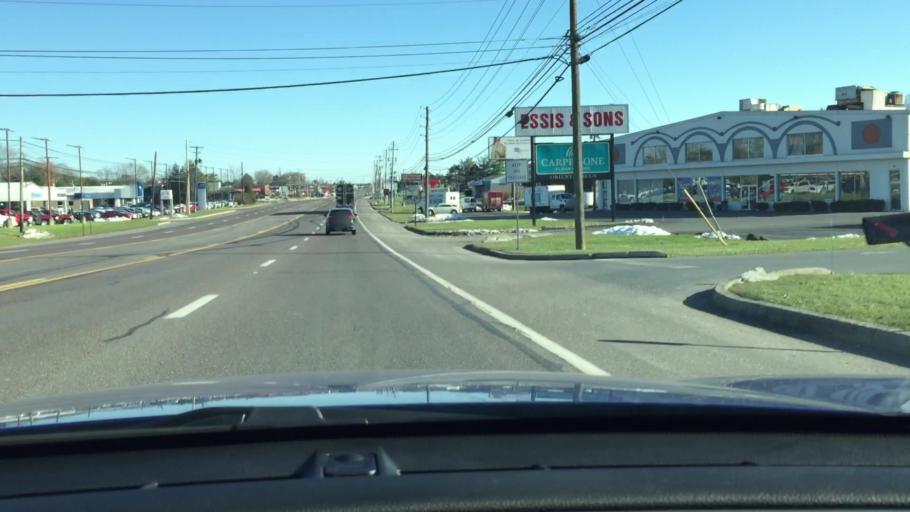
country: US
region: Pennsylvania
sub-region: Cumberland County
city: Mechanicsburg
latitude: 40.2450
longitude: -76.9971
